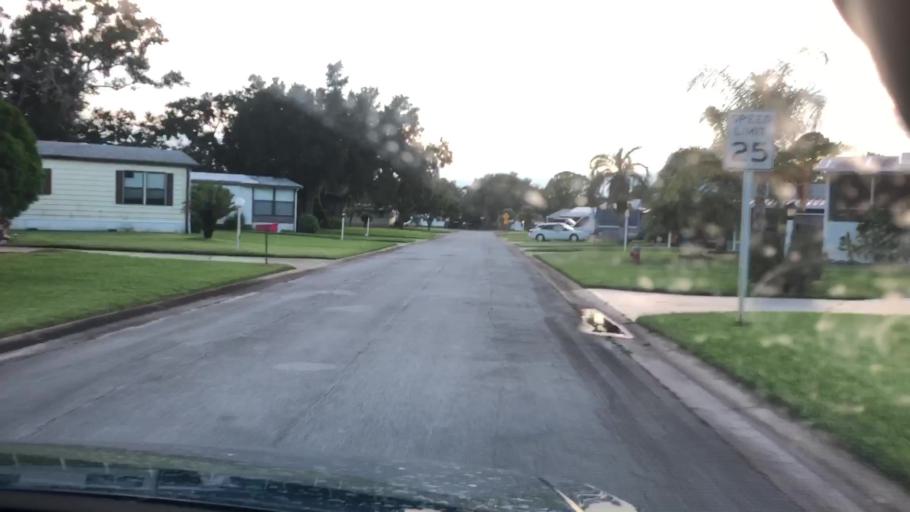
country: US
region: Florida
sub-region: Volusia County
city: Oak Hill
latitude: 28.9152
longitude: -80.8655
